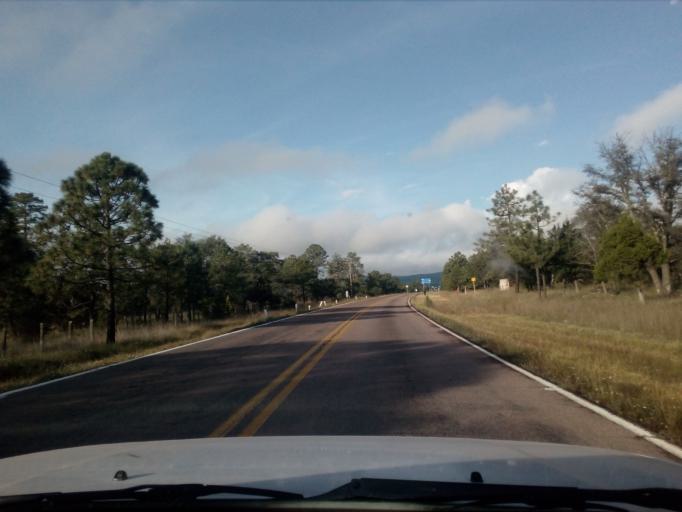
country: MX
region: Durango
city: Victoria de Durango
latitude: 23.9274
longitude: -104.9292
